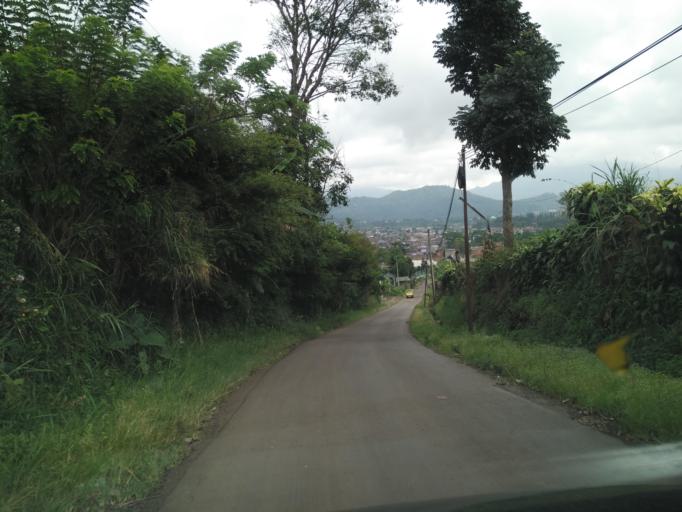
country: ID
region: West Java
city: Ciranjang-hilir
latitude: -6.7340
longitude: 107.0935
